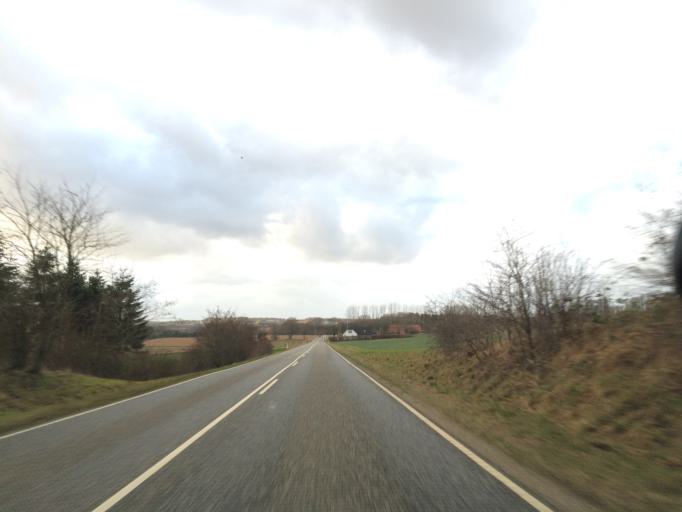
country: DK
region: Central Jutland
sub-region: Silkeborg Kommune
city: Svejbaek
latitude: 56.0964
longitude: 9.6195
